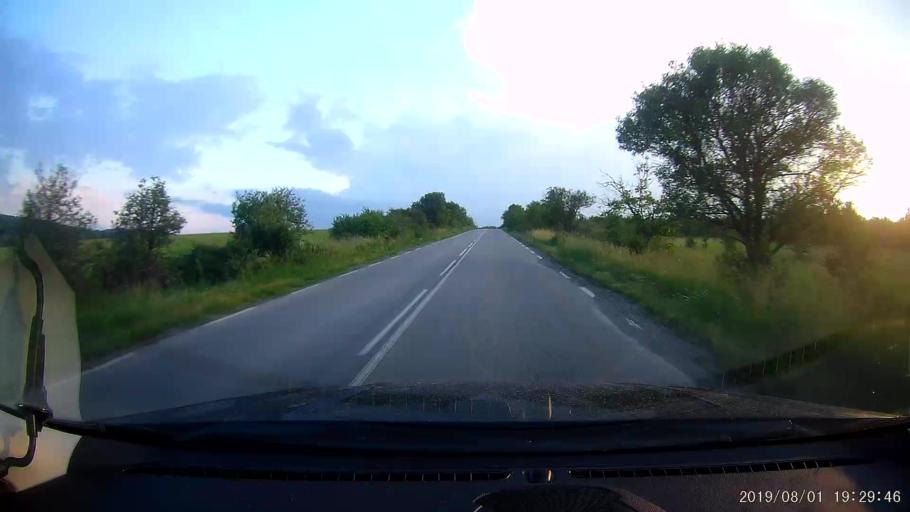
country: BG
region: Burgas
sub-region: Obshtina Sungurlare
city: Sungurlare
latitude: 42.8222
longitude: 26.9021
